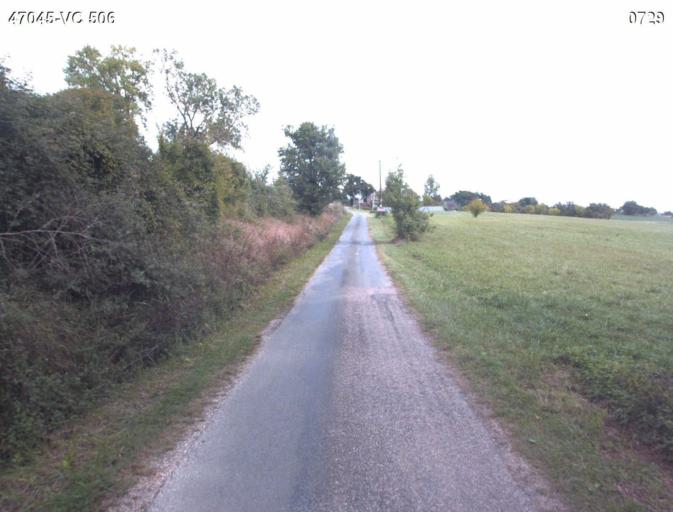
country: FR
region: Aquitaine
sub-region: Departement du Lot-et-Garonne
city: Nerac
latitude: 44.1279
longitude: 0.4101
